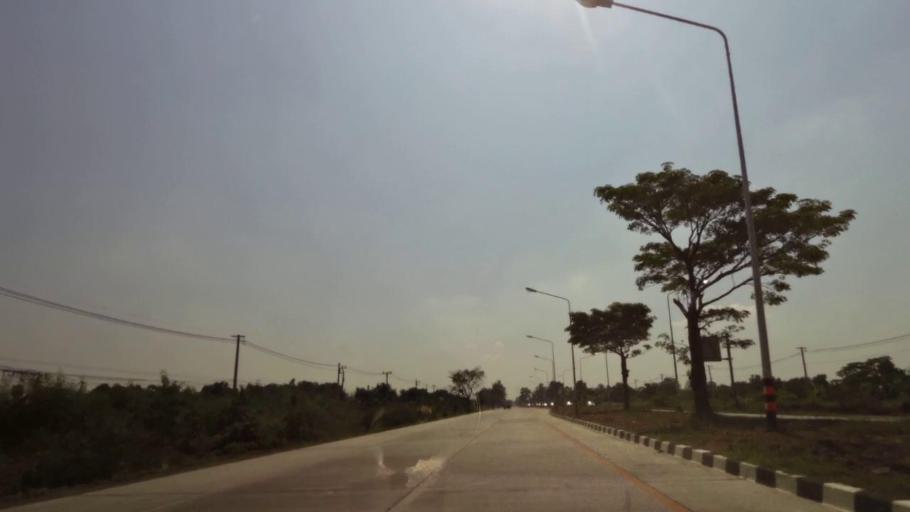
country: TH
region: Phichit
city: Bueng Na Rang
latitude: 16.2664
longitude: 100.1264
